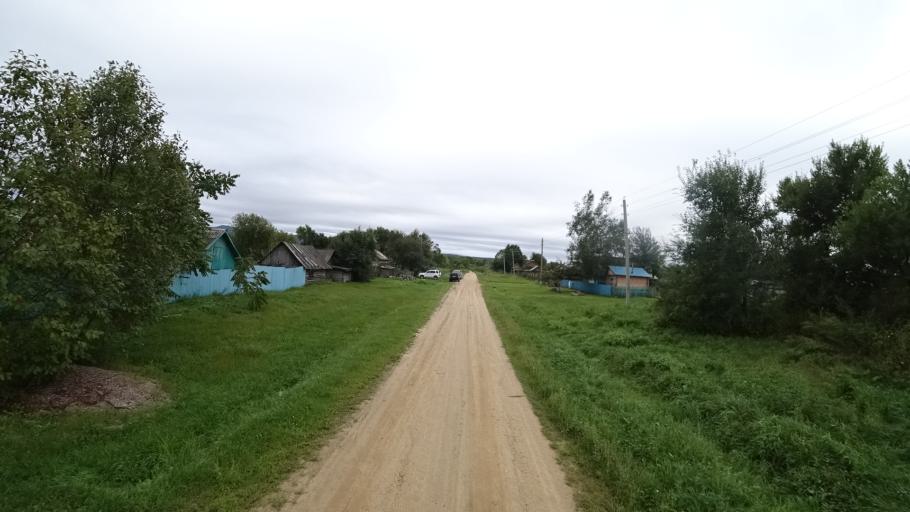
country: RU
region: Primorskiy
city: Rettikhovka
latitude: 44.1401
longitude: 132.6369
